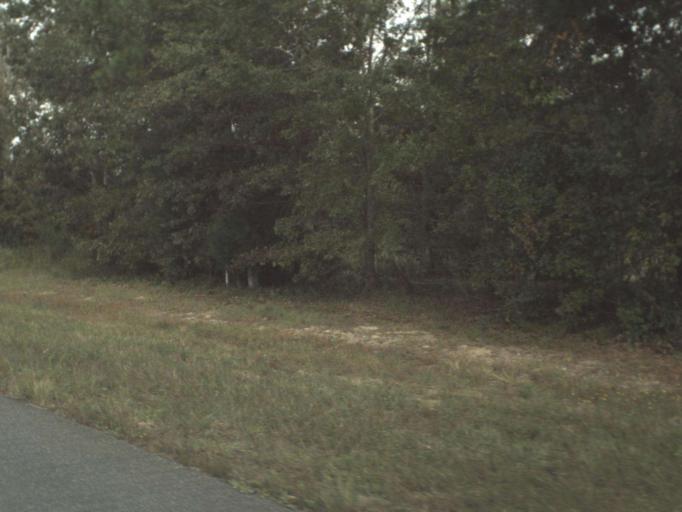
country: US
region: Florida
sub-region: Calhoun County
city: Blountstown
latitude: 30.4002
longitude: -85.2129
